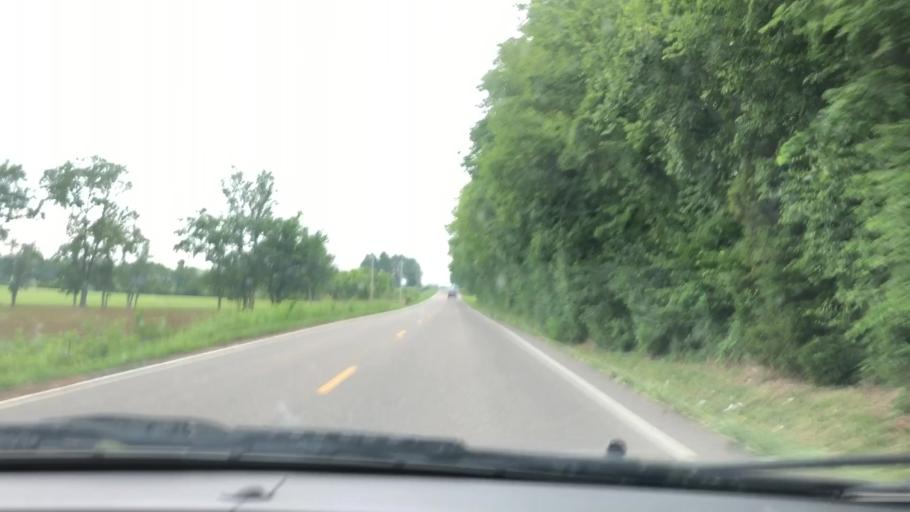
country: US
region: Tennessee
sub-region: Maury County
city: Spring Hill
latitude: 35.7435
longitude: -87.0095
